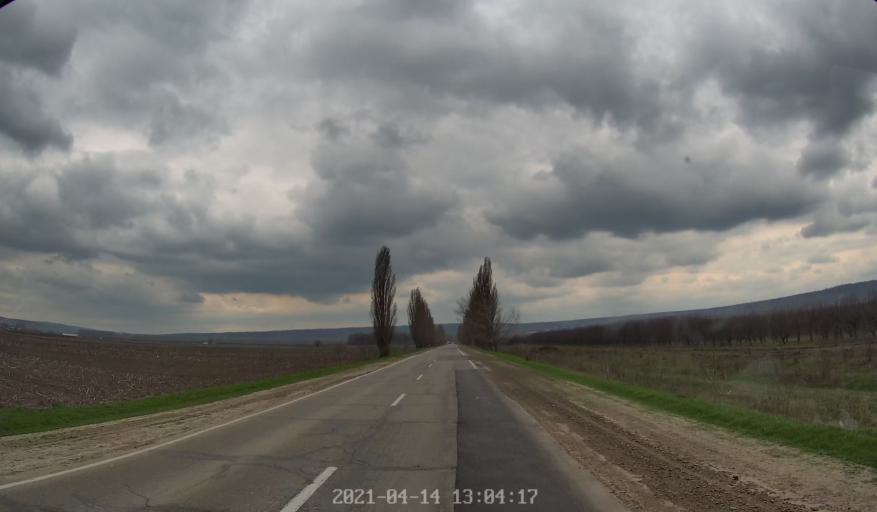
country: MD
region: Chisinau
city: Vadul lui Voda
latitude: 47.1087
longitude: 29.1021
